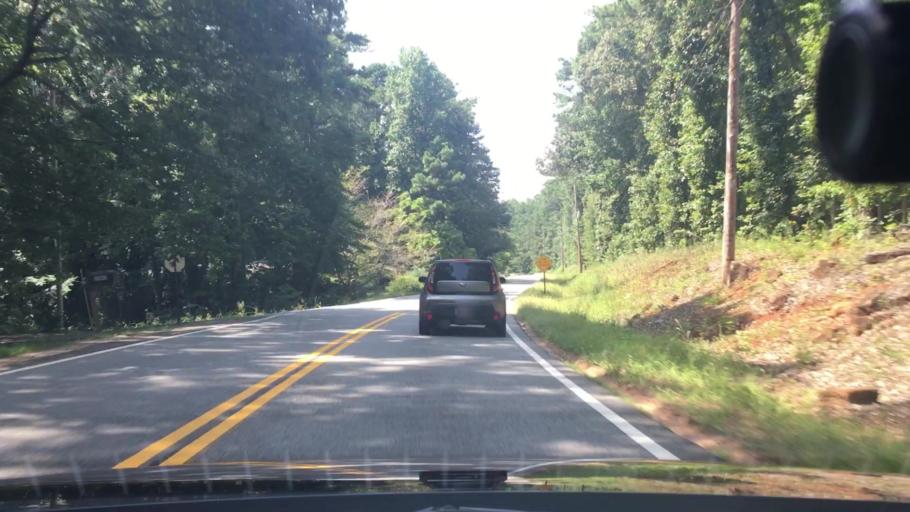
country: US
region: Georgia
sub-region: Coweta County
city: East Newnan
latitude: 33.3398
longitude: -84.7398
